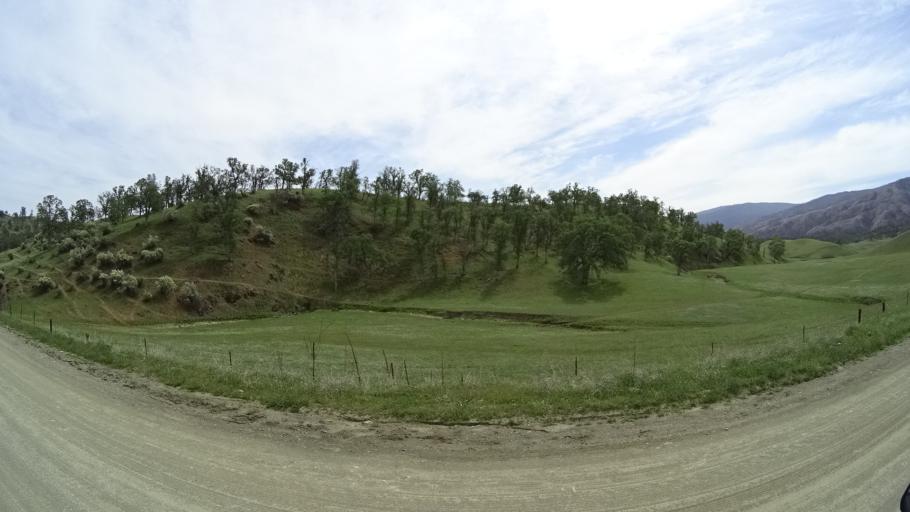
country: US
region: California
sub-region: Glenn County
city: Willows
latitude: 39.6275
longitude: -122.5921
